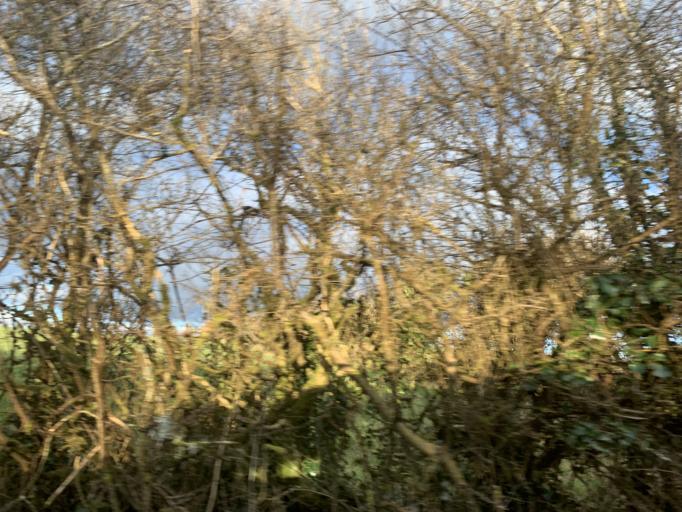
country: IE
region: Connaught
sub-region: Maigh Eo
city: Ballyhaunis
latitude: 53.8150
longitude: -8.6952
